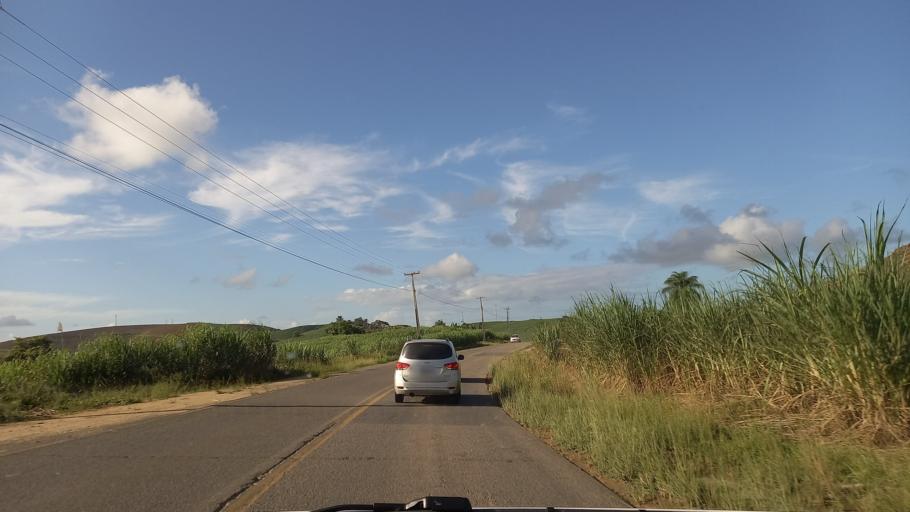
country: BR
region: Pernambuco
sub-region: Sirinhaem
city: Sirinhaem
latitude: -8.6111
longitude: -35.1193
